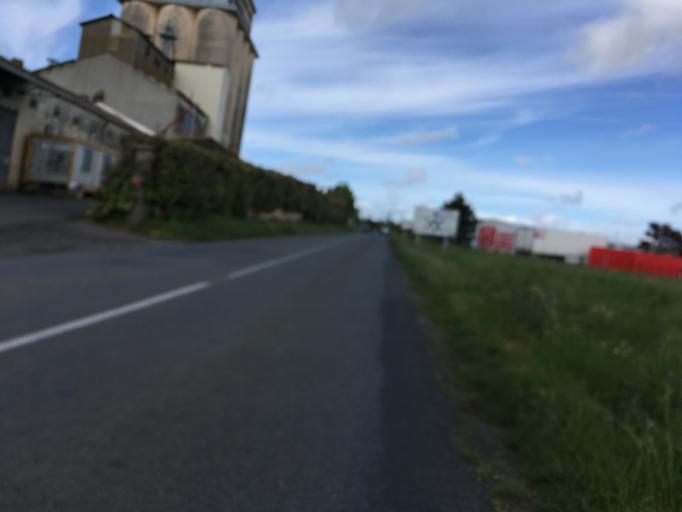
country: FR
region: Poitou-Charentes
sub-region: Departement de la Charente-Maritime
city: Dompierre-sur-Mer
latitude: 46.1738
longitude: -1.0684
